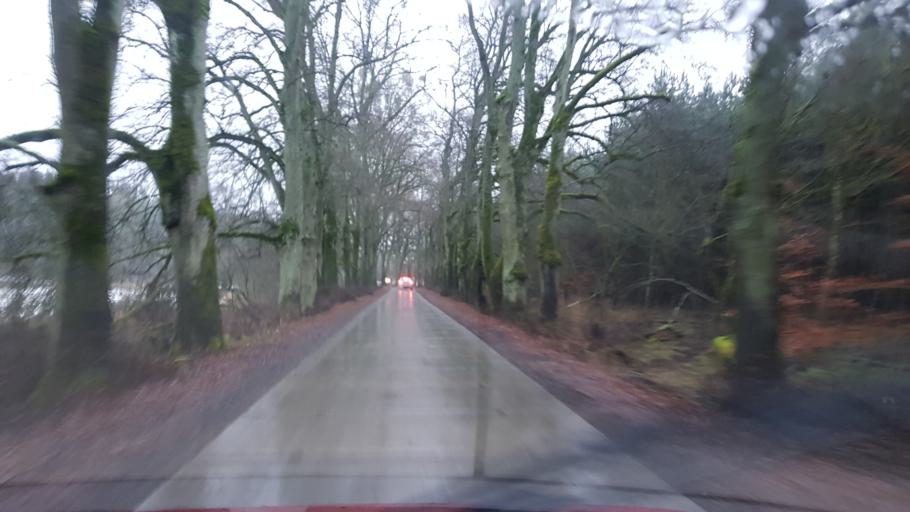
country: PL
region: West Pomeranian Voivodeship
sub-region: Powiat policki
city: Dobra
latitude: 53.5490
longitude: 14.4185
